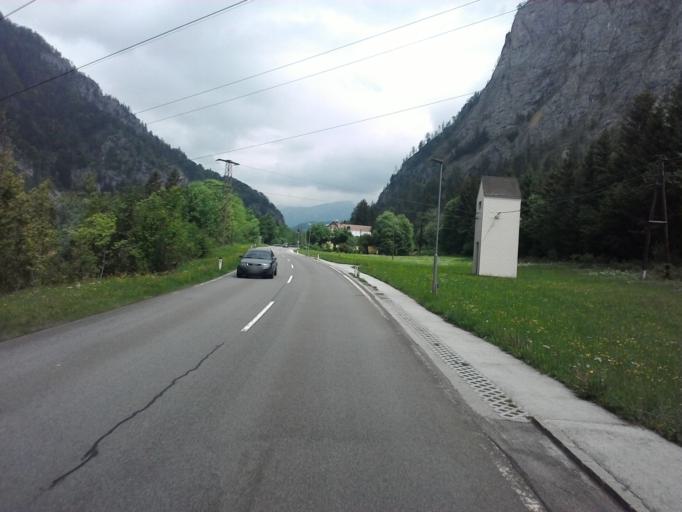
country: AT
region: Styria
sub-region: Politischer Bezirk Leoben
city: Hieflau
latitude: 47.6198
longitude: 14.7520
